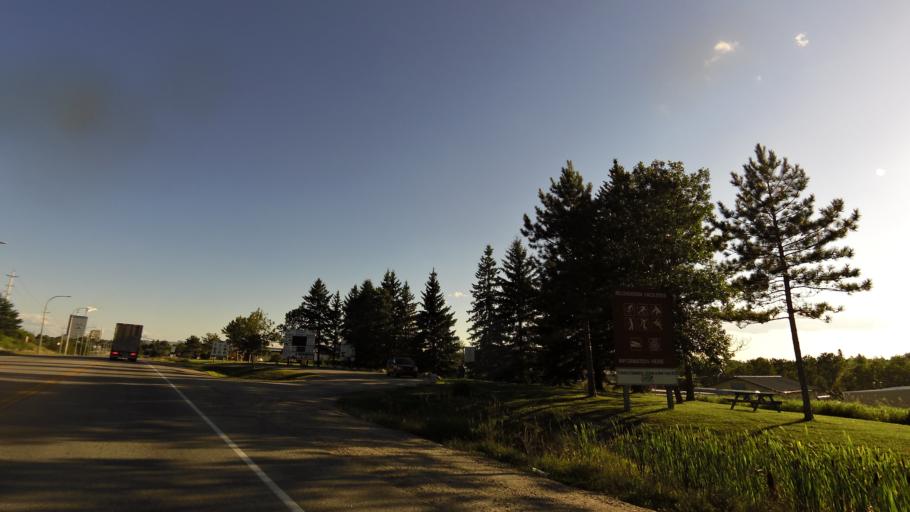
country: CA
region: Ontario
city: Dryden
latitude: 49.8002
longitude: -92.8475
